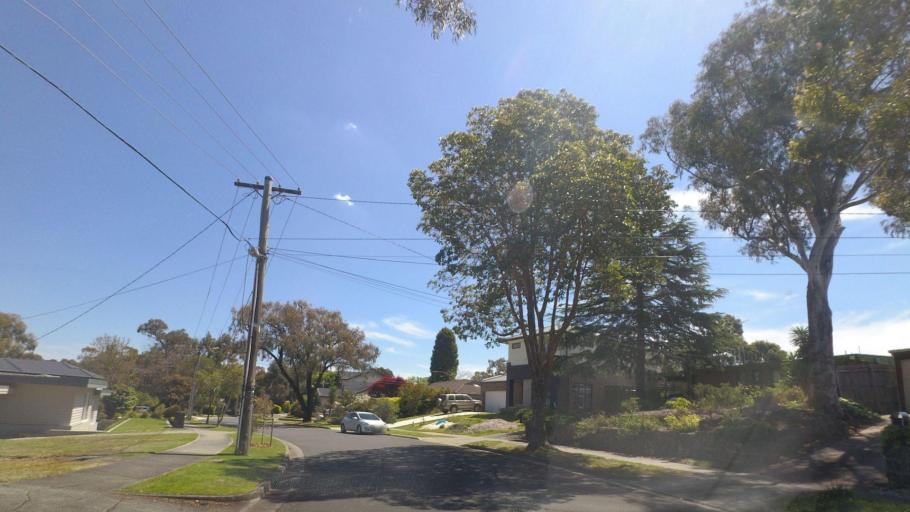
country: AU
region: Victoria
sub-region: Whitehorse
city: Vermont
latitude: -37.8447
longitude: 145.1960
